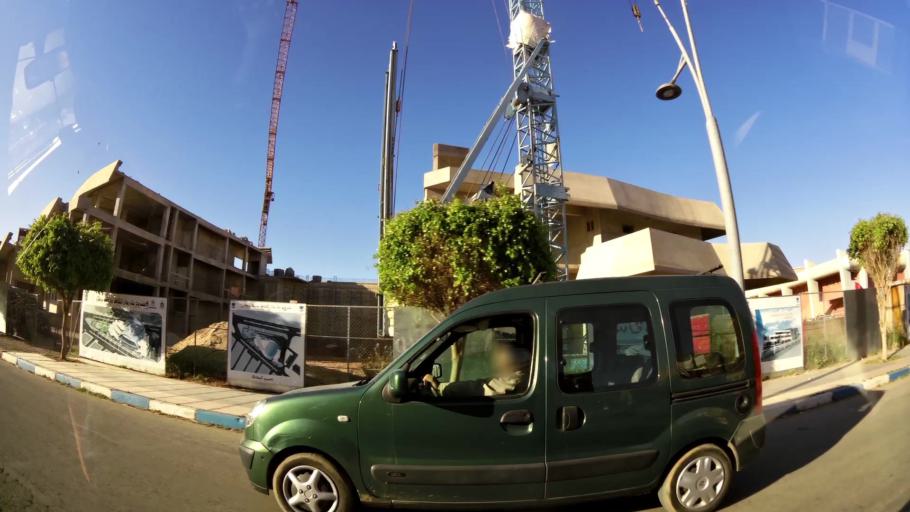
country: MA
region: Oriental
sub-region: Berkane-Taourirt
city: Berkane
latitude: 34.9335
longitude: -2.3235
